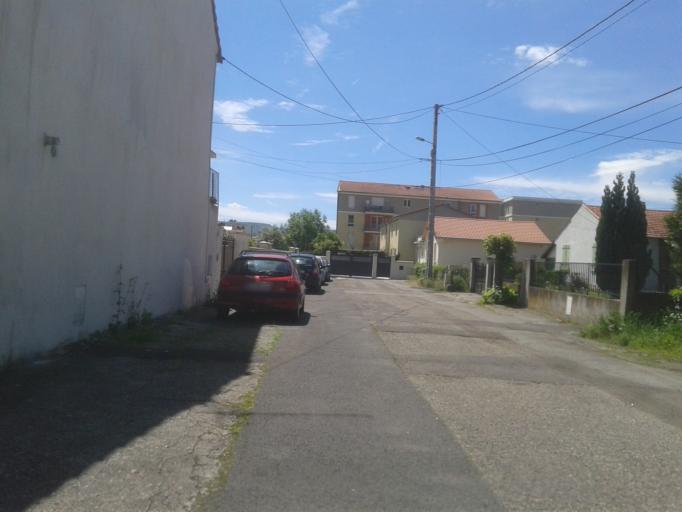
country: FR
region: Auvergne
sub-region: Departement du Puy-de-Dome
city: Clermont-Ferrand
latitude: 45.7887
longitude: 3.0923
